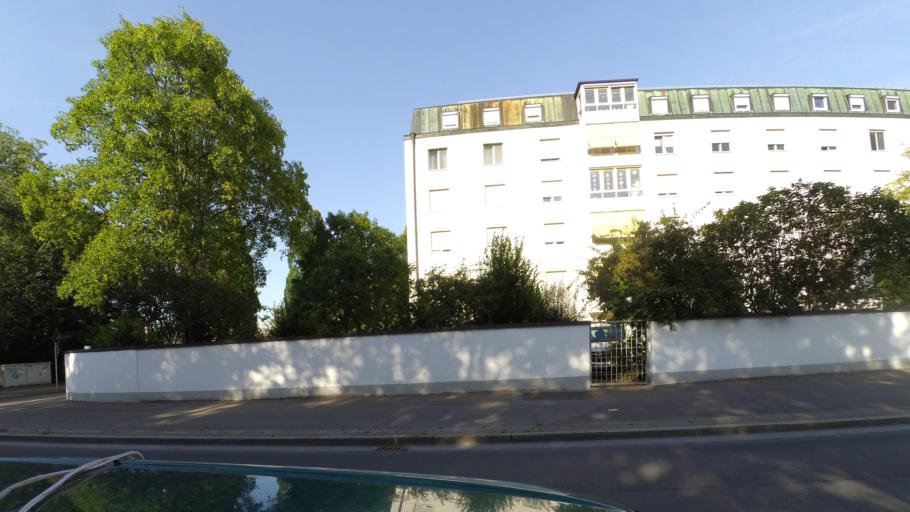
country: DE
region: Bavaria
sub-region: Swabia
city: Dillingen an der Donau
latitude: 48.5784
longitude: 10.4887
